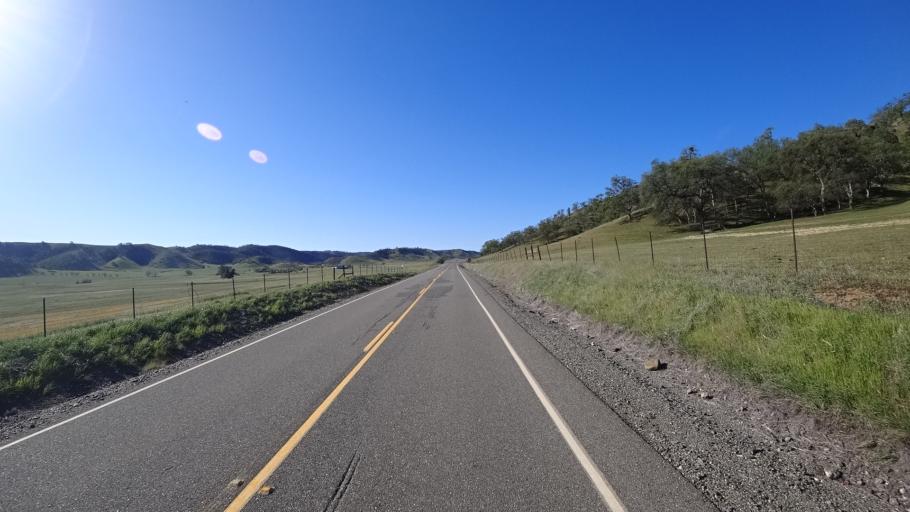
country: US
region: California
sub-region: Tehama County
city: Rancho Tehama Reserve
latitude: 39.7549
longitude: -122.5252
